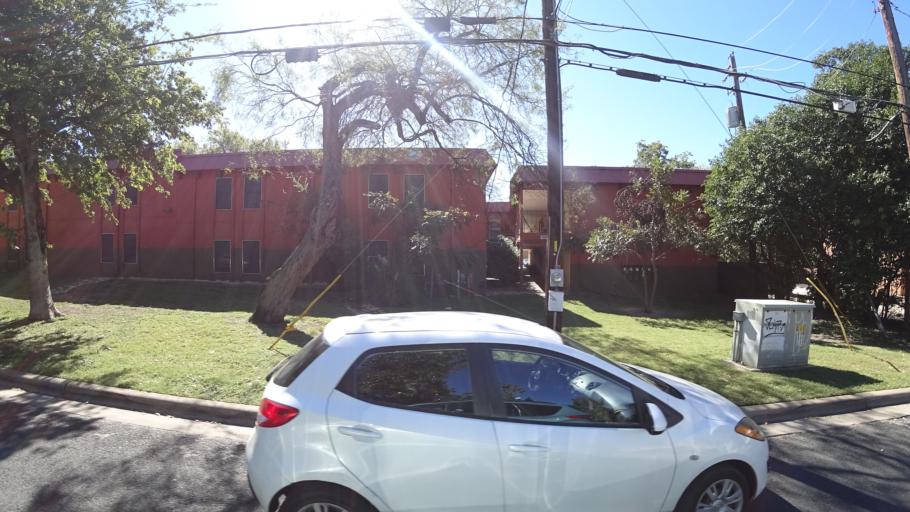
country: US
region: Texas
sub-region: Travis County
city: Austin
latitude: 30.3280
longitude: -97.7426
